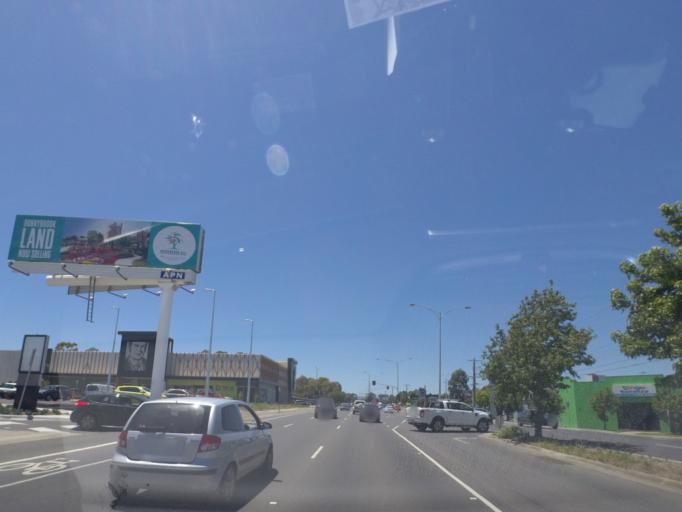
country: AU
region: Victoria
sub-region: Whittlesea
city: Lalor
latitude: -37.6560
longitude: 145.0209
